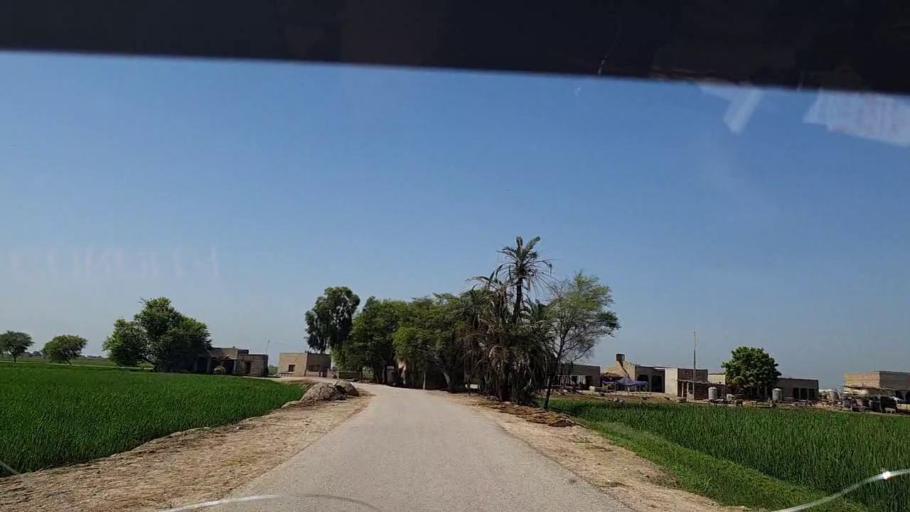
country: PK
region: Sindh
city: Kandhkot
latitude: 28.3098
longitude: 69.1046
